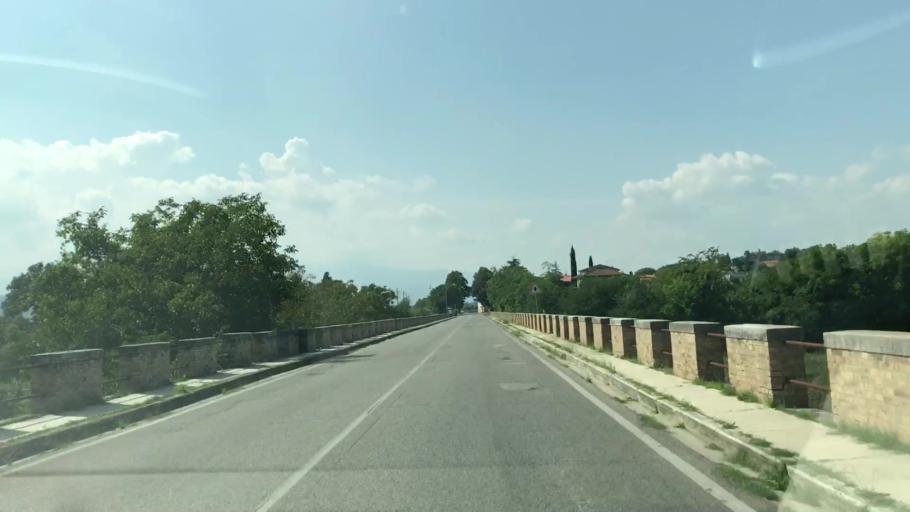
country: IT
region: The Marches
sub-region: Provincia di Ascoli Piceno
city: Monsampolo del Tronto
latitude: 42.8821
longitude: 13.7935
